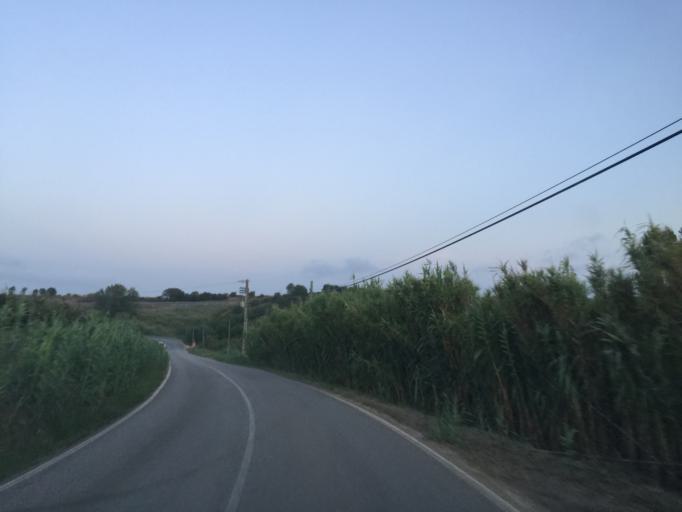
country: PT
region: Leiria
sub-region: Bombarral
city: Bombarral
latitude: 39.2728
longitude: -9.1714
